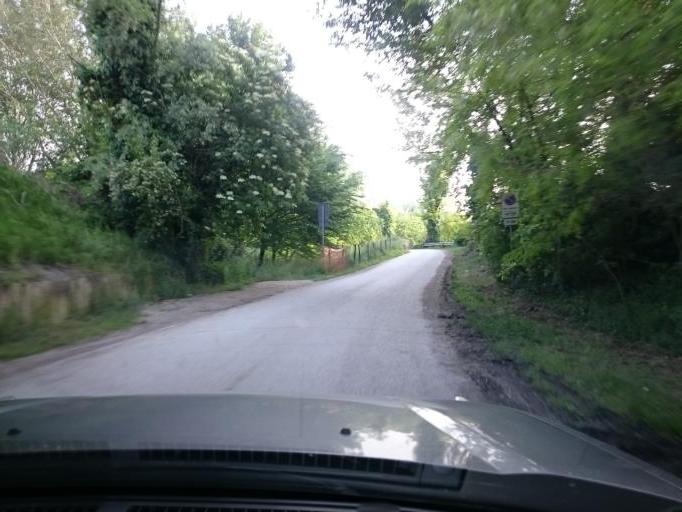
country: IT
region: Veneto
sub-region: Provincia di Padova
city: Noventa
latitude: 45.4027
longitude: 11.9237
